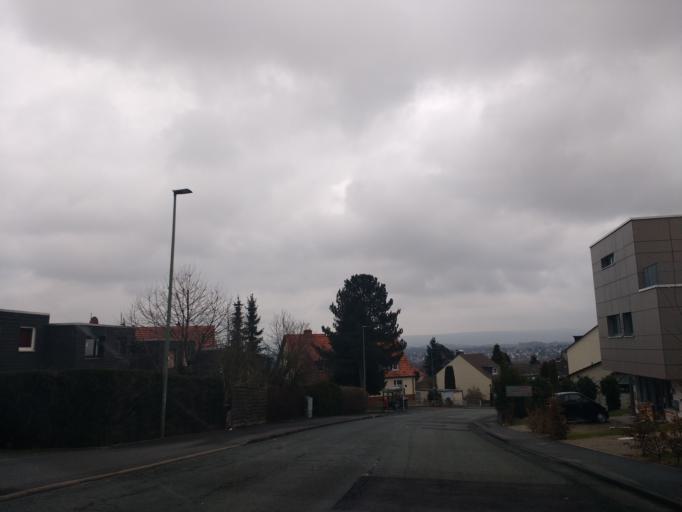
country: DE
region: Hesse
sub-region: Regierungsbezirk Kassel
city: Baunatal
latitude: 51.2824
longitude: 9.4243
